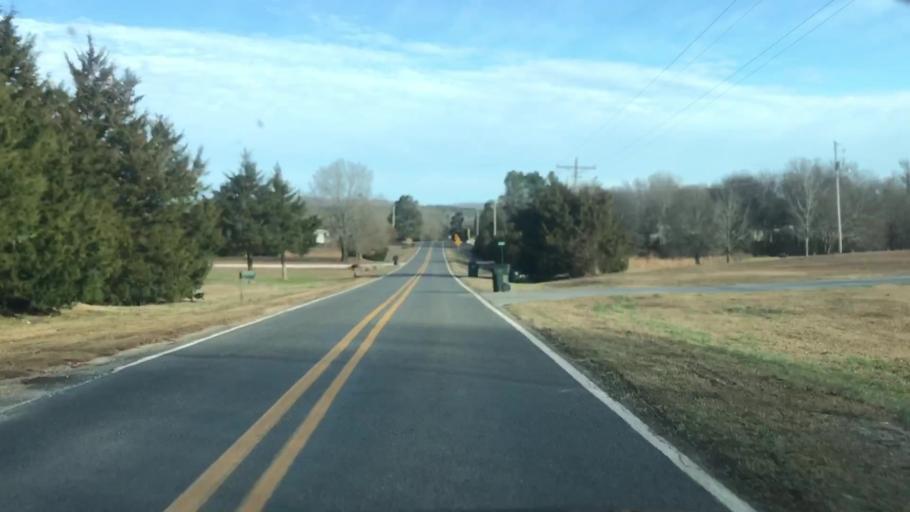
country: US
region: Arkansas
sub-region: Garland County
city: Rockwell
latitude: 34.5051
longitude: -93.2762
